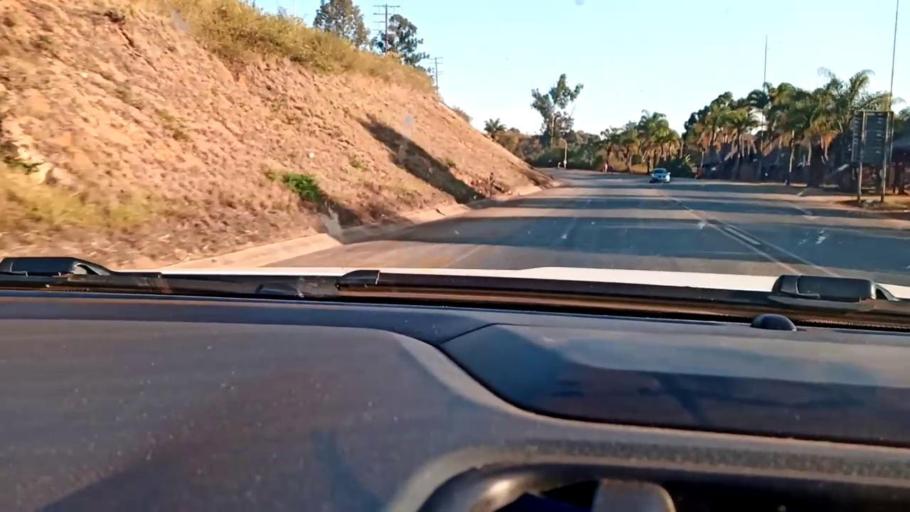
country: ZA
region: Limpopo
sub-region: Mopani District Municipality
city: Duiwelskloof
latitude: -23.6892
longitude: 30.1470
